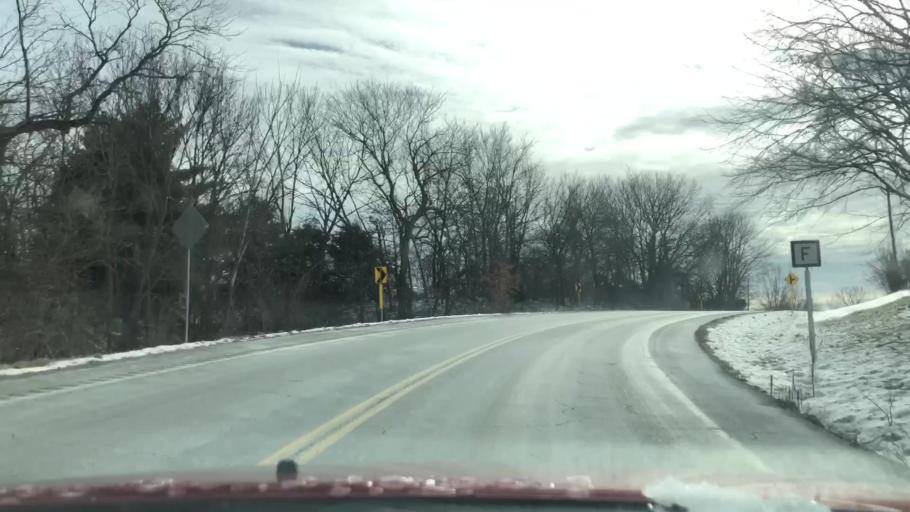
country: US
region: Missouri
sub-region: Jackson County
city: Lone Jack
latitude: 38.8920
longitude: -94.1345
